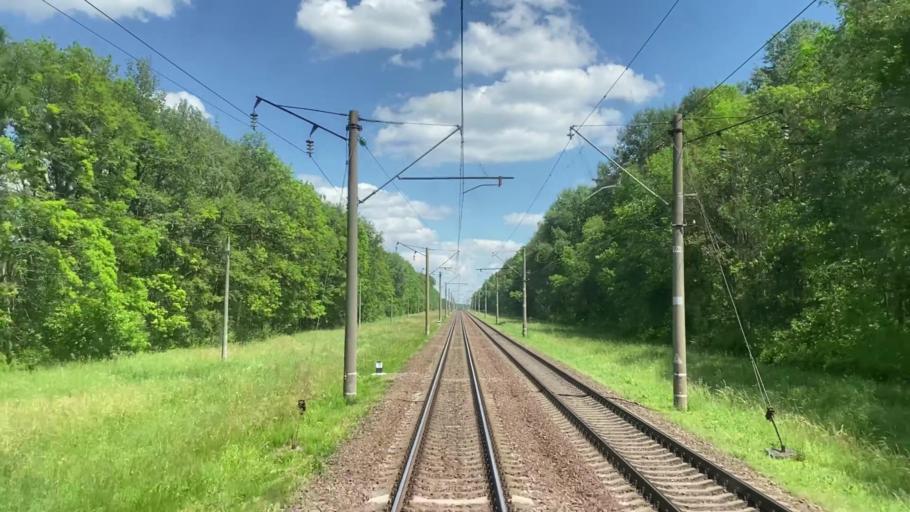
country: BY
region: Brest
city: Pruzhany
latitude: 52.4941
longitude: 24.5993
